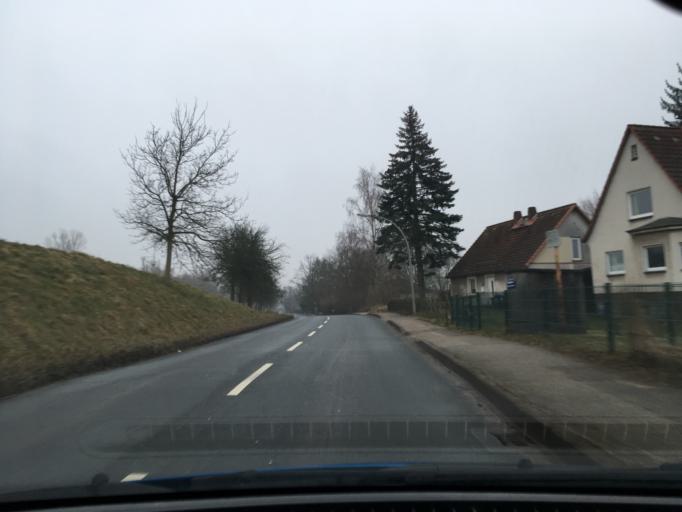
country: DE
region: Hamburg
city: Altona
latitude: 53.4988
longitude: 9.8994
